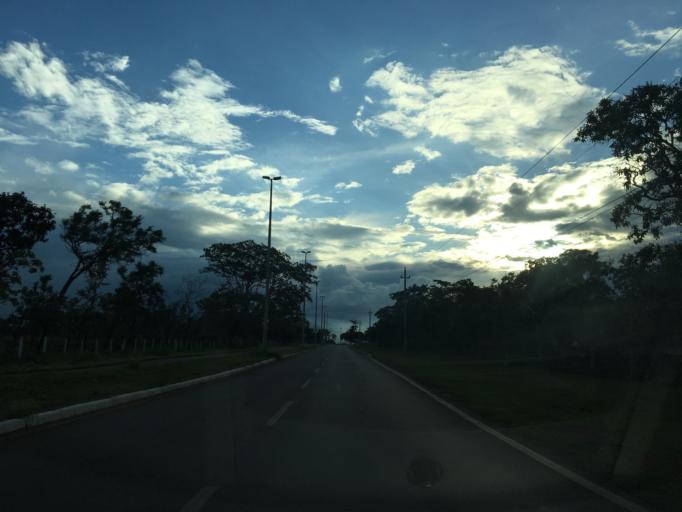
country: BR
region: Federal District
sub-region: Brasilia
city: Brasilia
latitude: -15.8047
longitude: -47.8359
